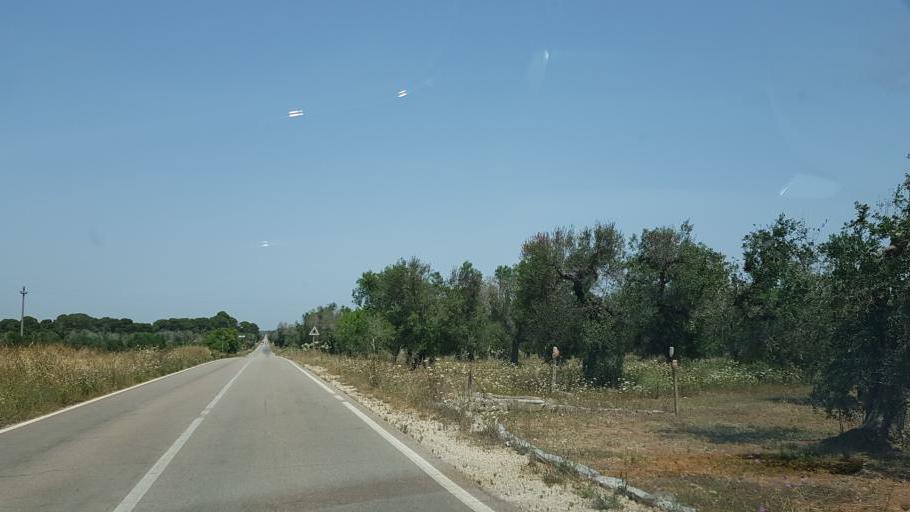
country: IT
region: Apulia
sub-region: Provincia di Lecce
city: Porto Cesareo
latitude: 40.3035
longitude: 17.9179
